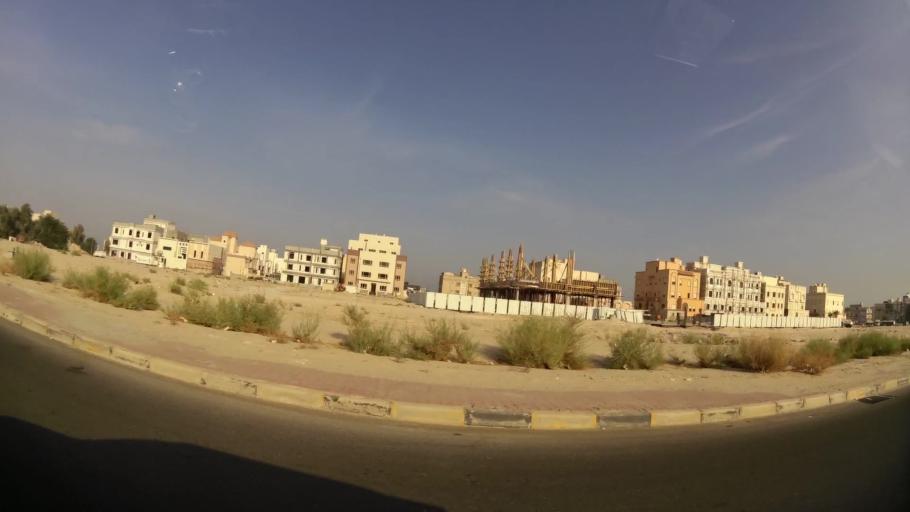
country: KW
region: Mubarak al Kabir
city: Mubarak al Kabir
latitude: 29.1898
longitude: 48.1062
